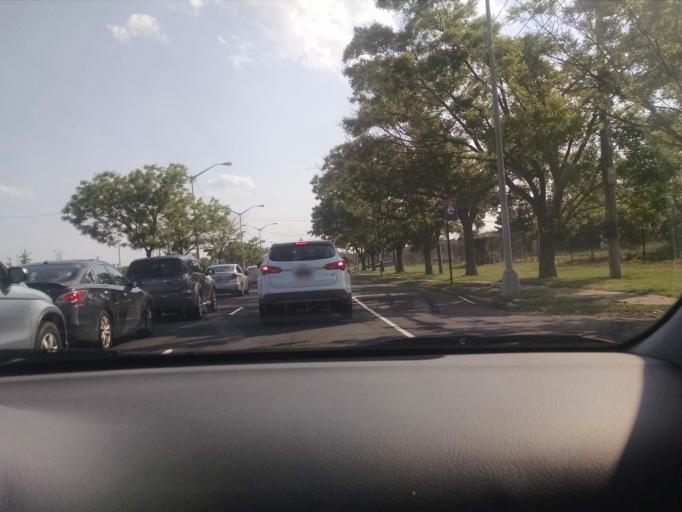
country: US
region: New York
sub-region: Richmond County
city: Staten Island
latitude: 40.5804
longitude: -74.0767
